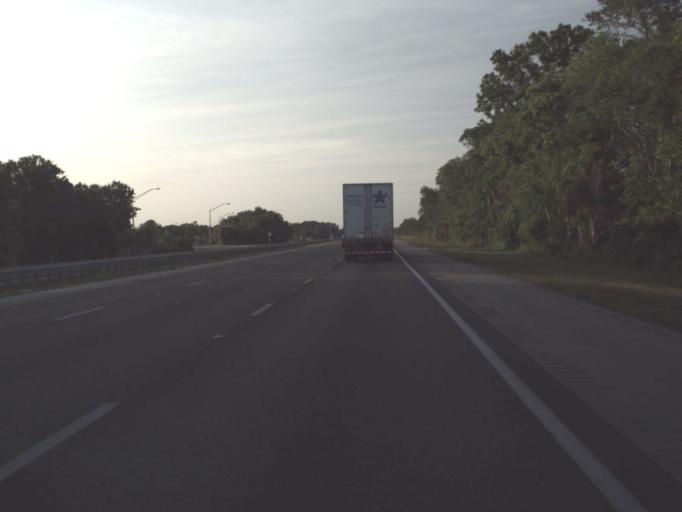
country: US
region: Florida
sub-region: Brevard County
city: Mims
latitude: 28.7040
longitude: -80.8851
